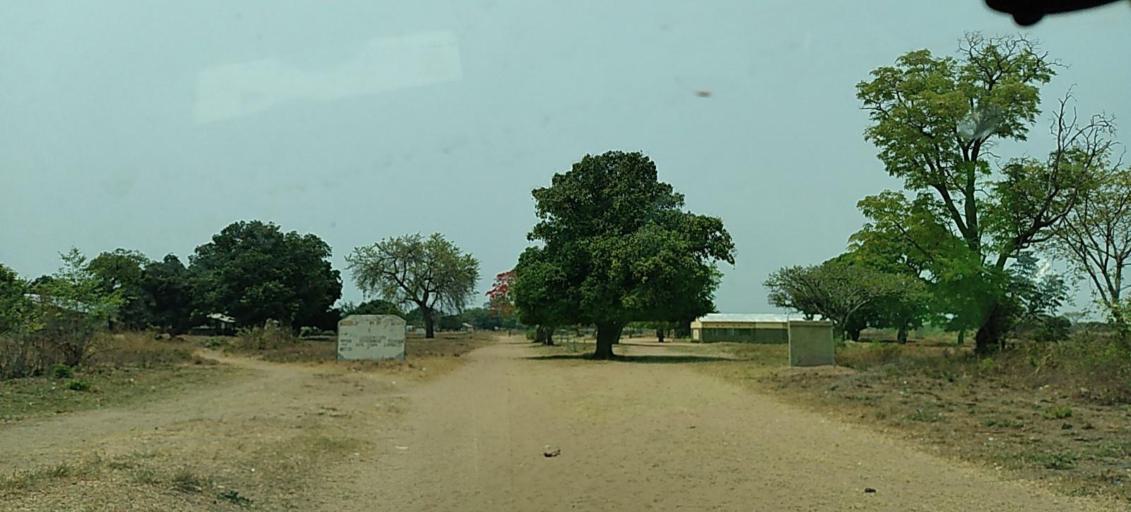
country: ZM
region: Western
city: Lukulu
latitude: -14.1598
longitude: 23.3176
